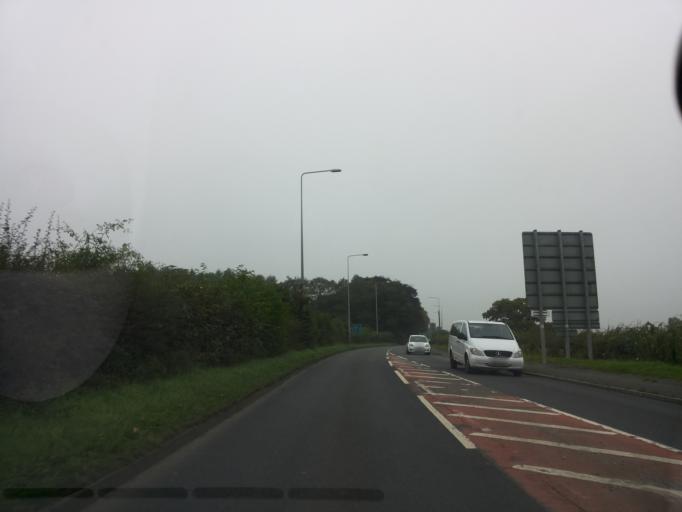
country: GB
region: England
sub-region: Lancashire
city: Langho
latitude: 53.8085
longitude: -2.4472
